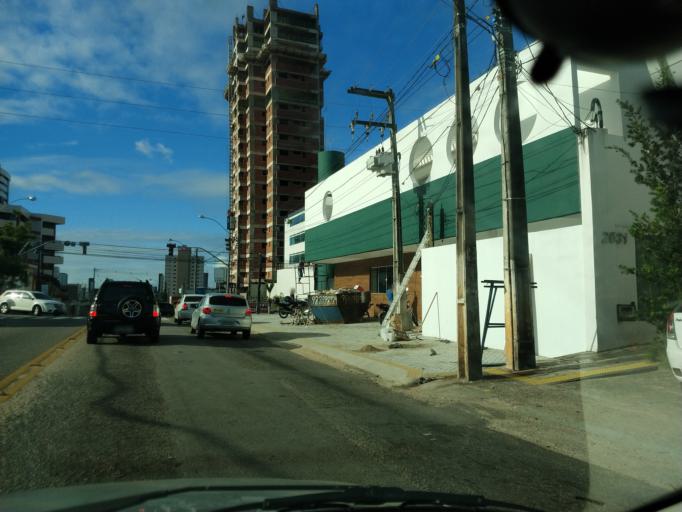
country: BR
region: Rio Grande do Norte
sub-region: Natal
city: Natal
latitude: -5.8301
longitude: -35.2224
